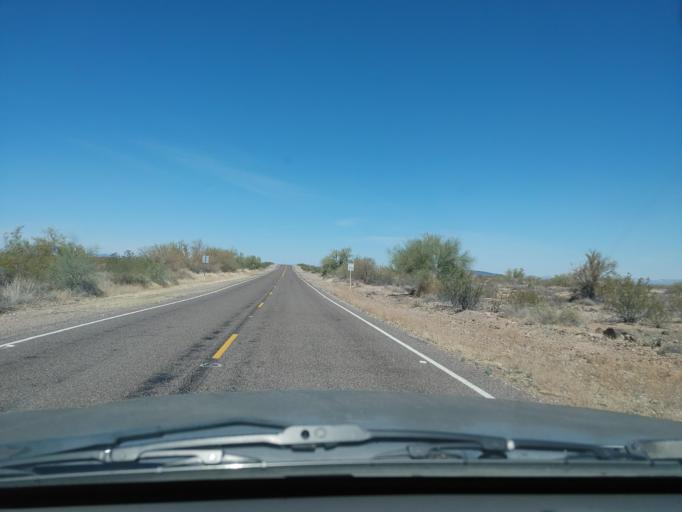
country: US
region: Arizona
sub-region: Maricopa County
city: Gila Bend
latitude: 32.8989
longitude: -113.2536
